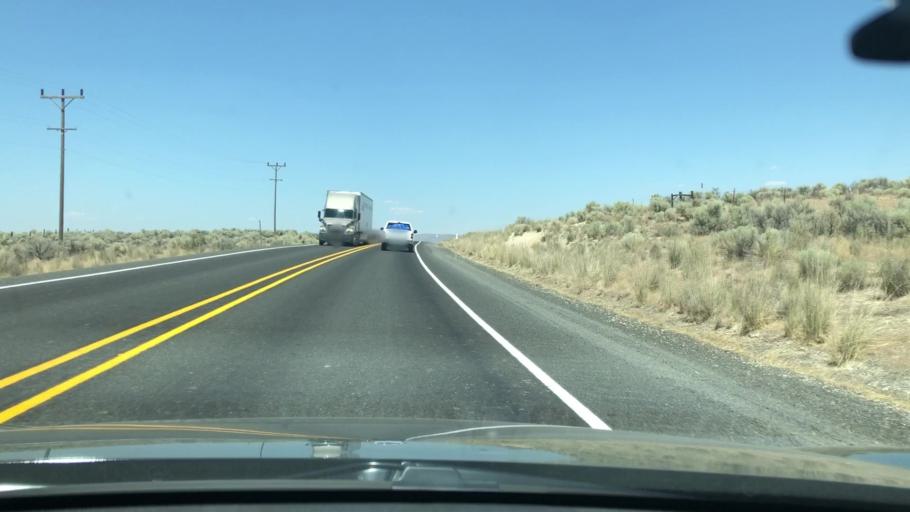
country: US
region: Idaho
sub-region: Owyhee County
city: Murphy
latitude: 42.9963
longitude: -117.0615
